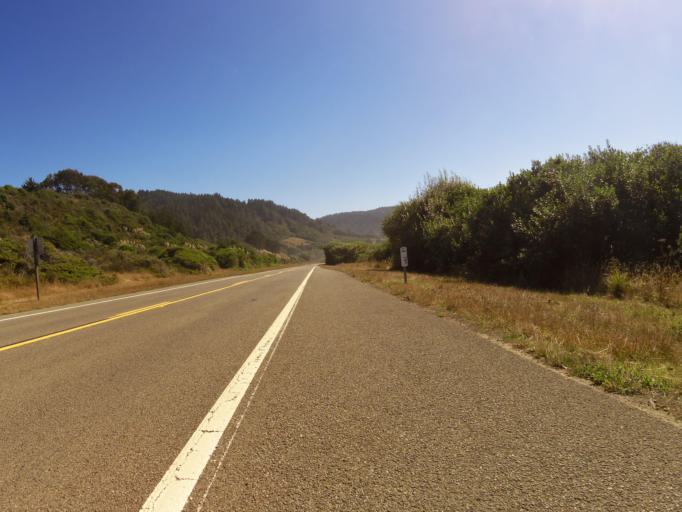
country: US
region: California
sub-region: Mendocino County
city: Fort Bragg
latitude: 39.6631
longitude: -123.7869
